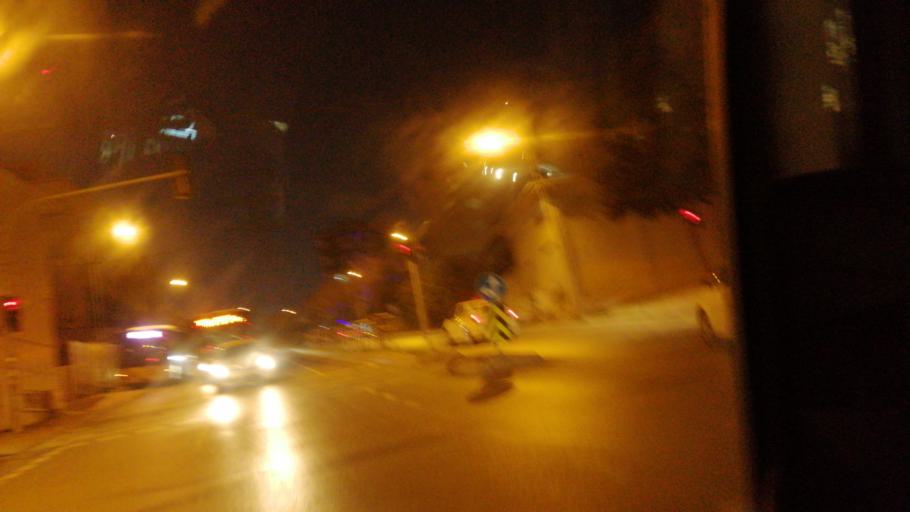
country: TR
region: Istanbul
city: Umraniye
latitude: 41.0045
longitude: 29.1358
